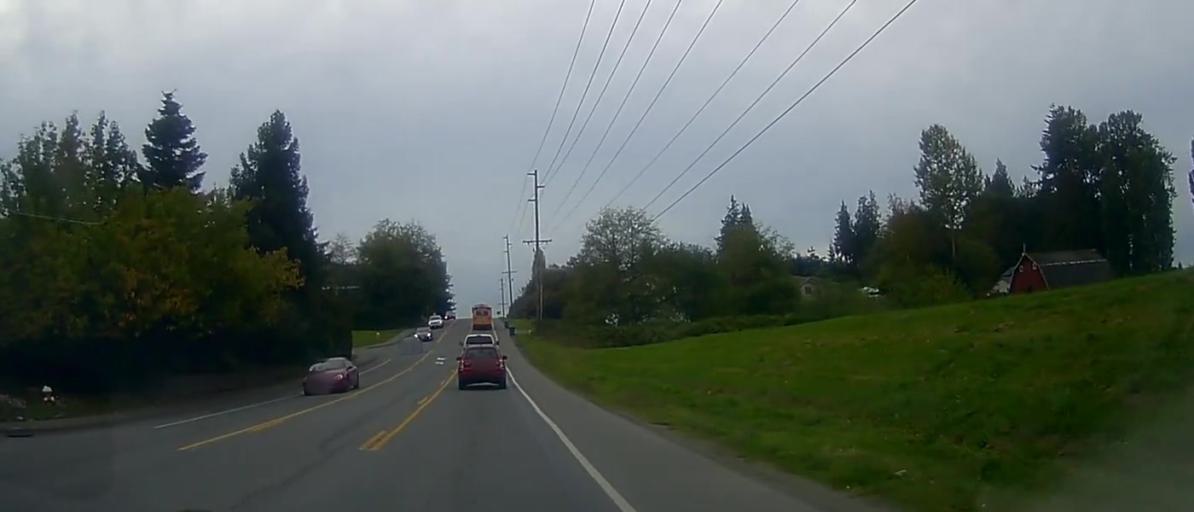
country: US
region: Washington
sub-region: Skagit County
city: Mount Vernon
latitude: 48.4430
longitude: -122.3204
